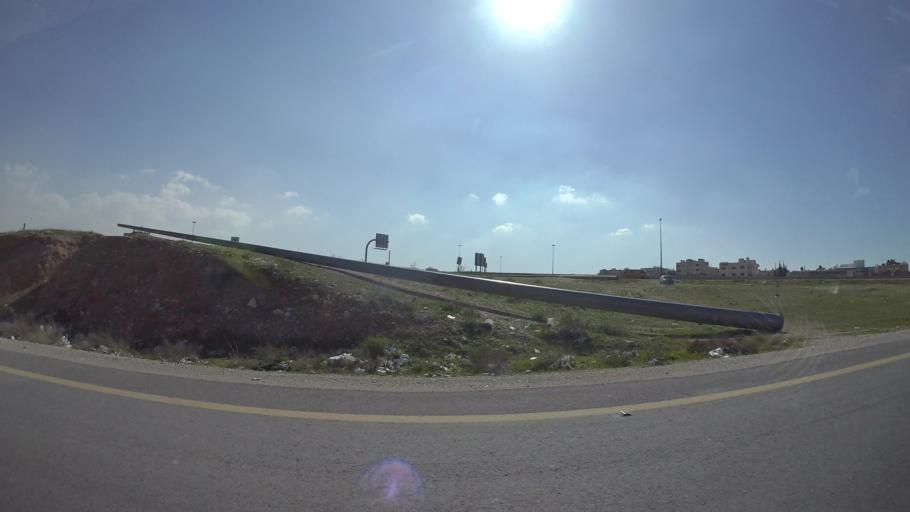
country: JO
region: Zarqa
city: Russeifa
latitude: 32.0212
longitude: 36.0776
